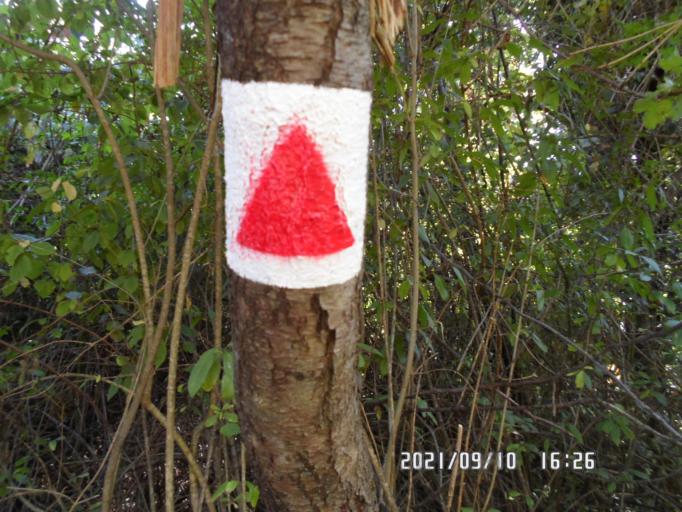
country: HU
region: Zala
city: Pacsa
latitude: 46.5881
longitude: 17.0495
